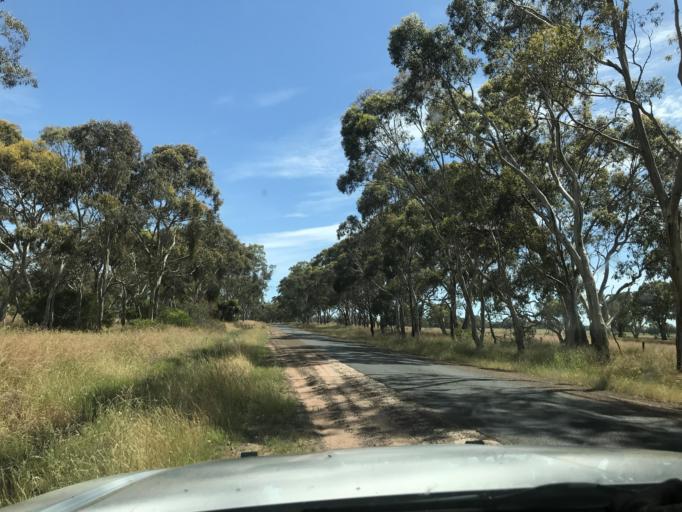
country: AU
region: Victoria
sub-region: Horsham
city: Horsham
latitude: -37.0567
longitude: 141.5751
